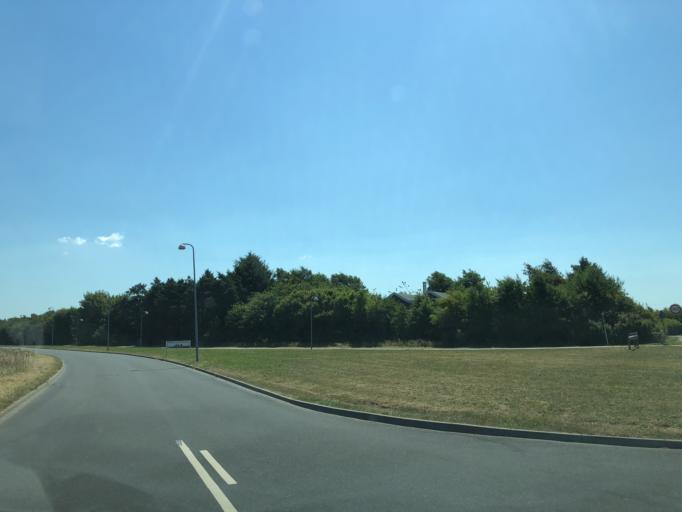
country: DK
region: Central Jutland
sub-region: Holstebro Kommune
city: Holstebro
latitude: 56.3618
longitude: 8.6763
